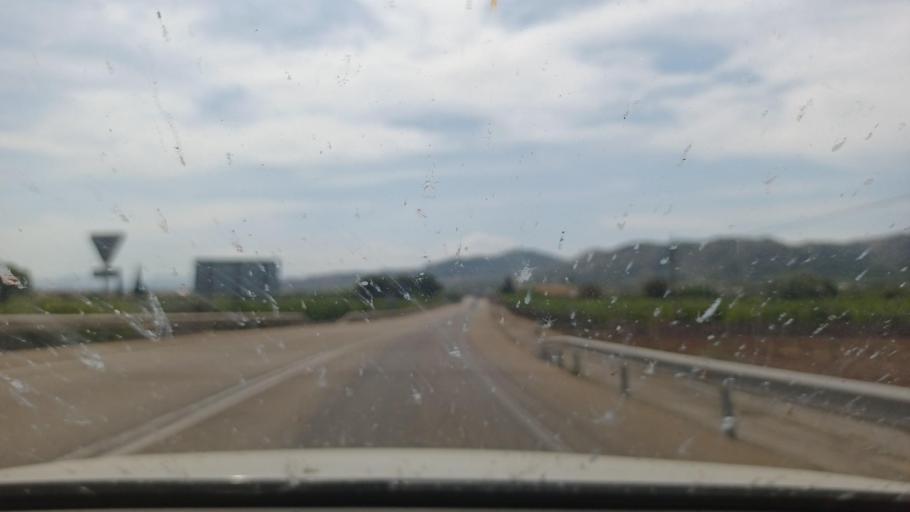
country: ES
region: Valencia
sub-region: Provincia de Castello
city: Castello de la Plana
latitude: 40.0256
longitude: -0.0103
